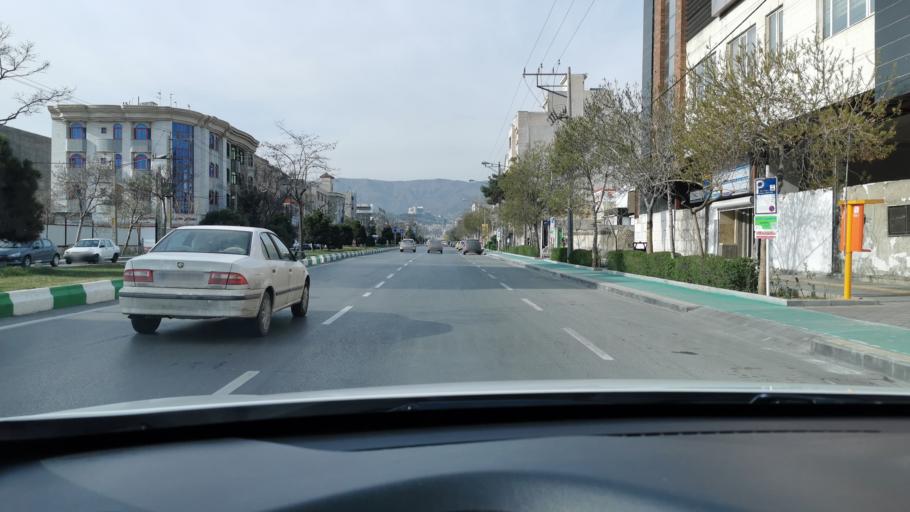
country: IR
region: Razavi Khorasan
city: Mashhad
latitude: 36.3188
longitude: 59.5116
